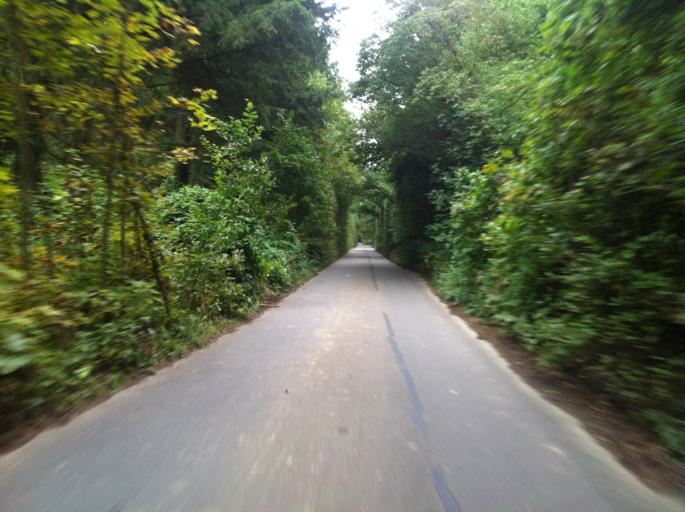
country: DE
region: Rheinland-Pfalz
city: Essenheim
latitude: 49.9541
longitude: 8.1660
